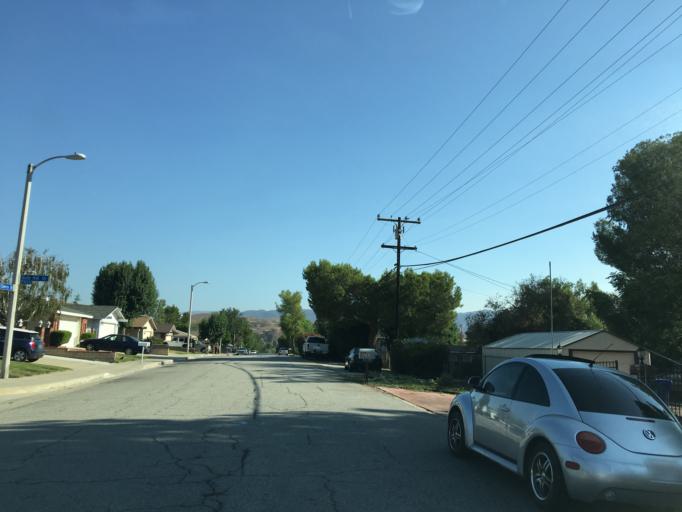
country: US
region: California
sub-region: Los Angeles County
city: Castaic
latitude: 34.4895
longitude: -118.6256
